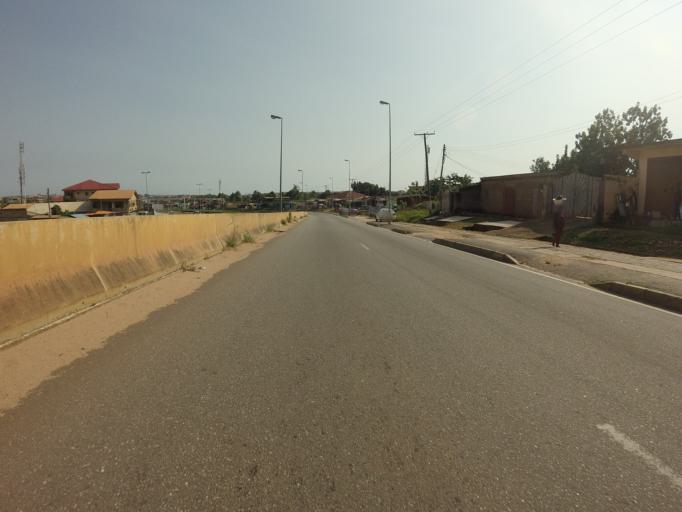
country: GH
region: Greater Accra
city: Gbawe
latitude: 5.6096
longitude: -0.2972
